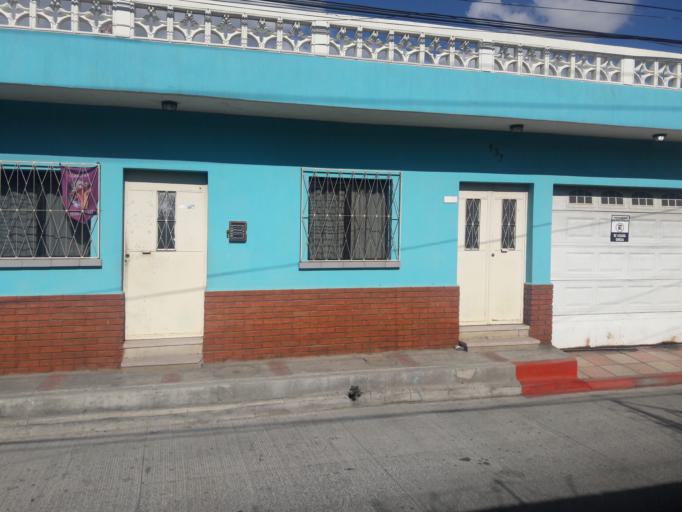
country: GT
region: Guatemala
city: Amatitlan
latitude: 14.4776
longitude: -90.6221
